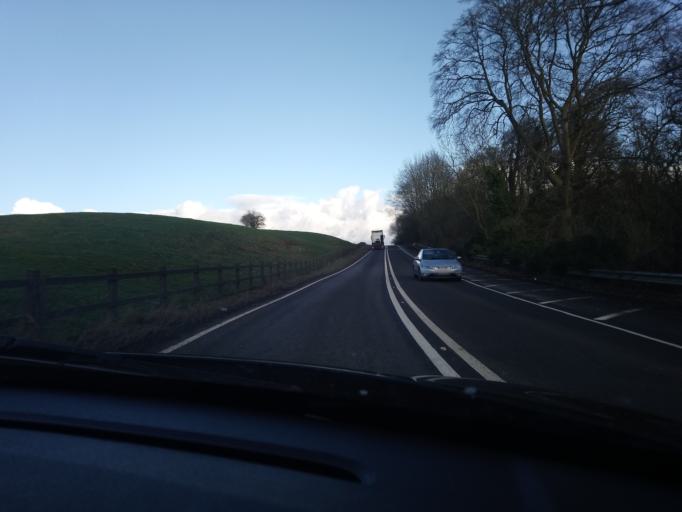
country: GB
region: England
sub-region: Shropshire
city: Ellesmere
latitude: 52.9033
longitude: -2.8717
